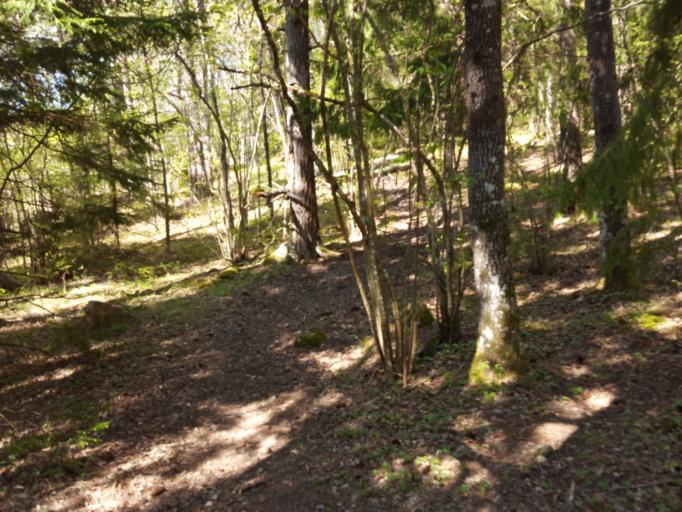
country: SE
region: Uppsala
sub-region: Uppsala Kommun
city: Storvreta
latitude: 59.9018
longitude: 17.7431
